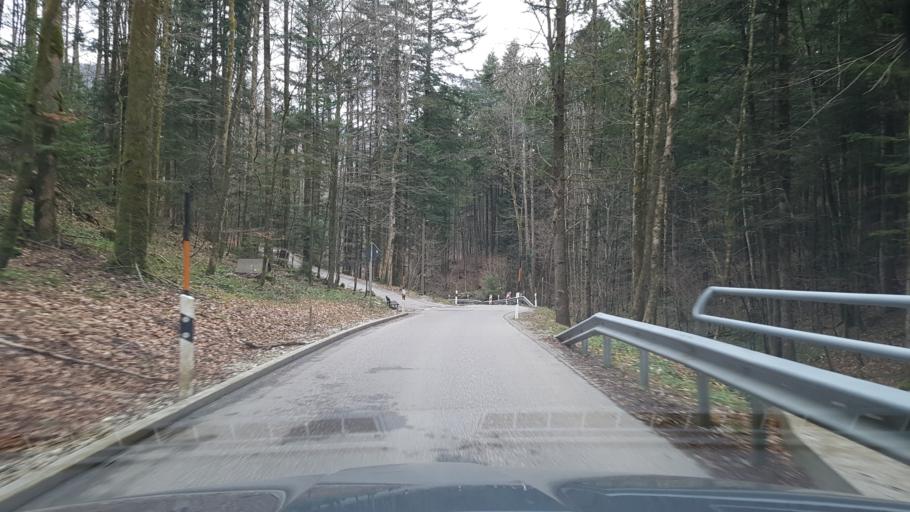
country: DE
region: Bavaria
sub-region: Upper Bavaria
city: Marktschellenberg
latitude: 47.6856
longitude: 13.0558
